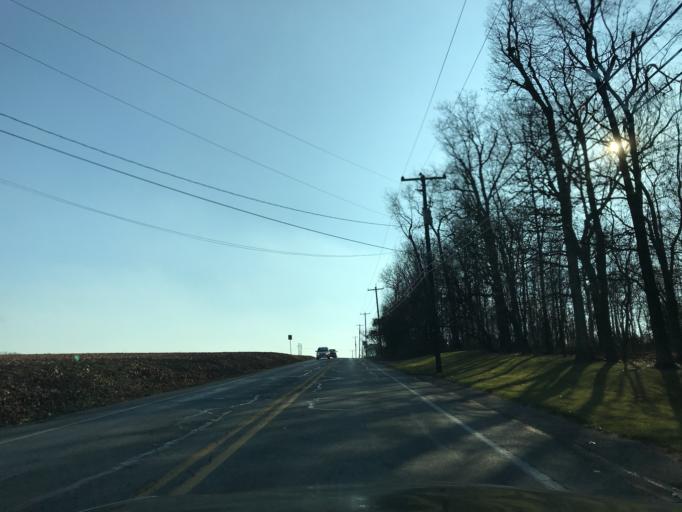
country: US
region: Pennsylvania
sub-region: York County
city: Shrewsbury
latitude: 39.7930
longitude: -76.6784
